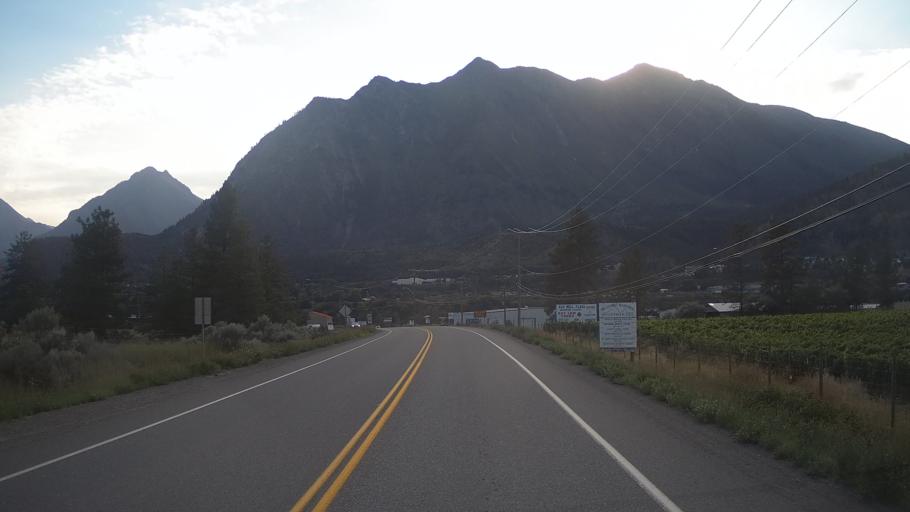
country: CA
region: British Columbia
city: Lillooet
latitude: 50.6859
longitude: -121.9213
